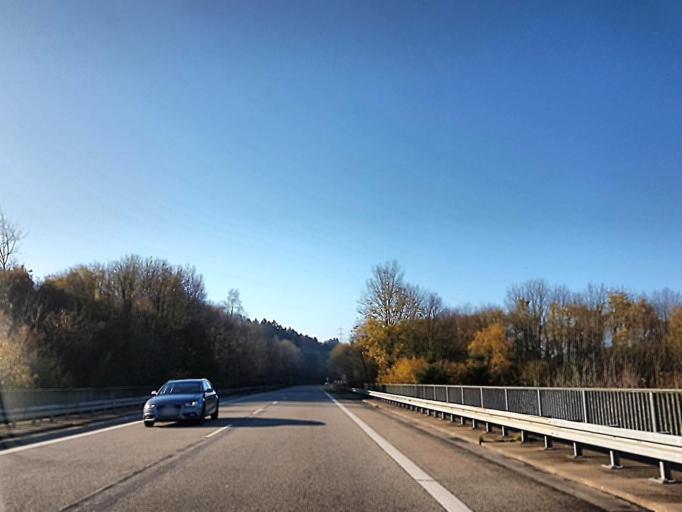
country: DE
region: North Rhine-Westphalia
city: Radevormwald
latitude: 51.1958
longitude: 7.3041
